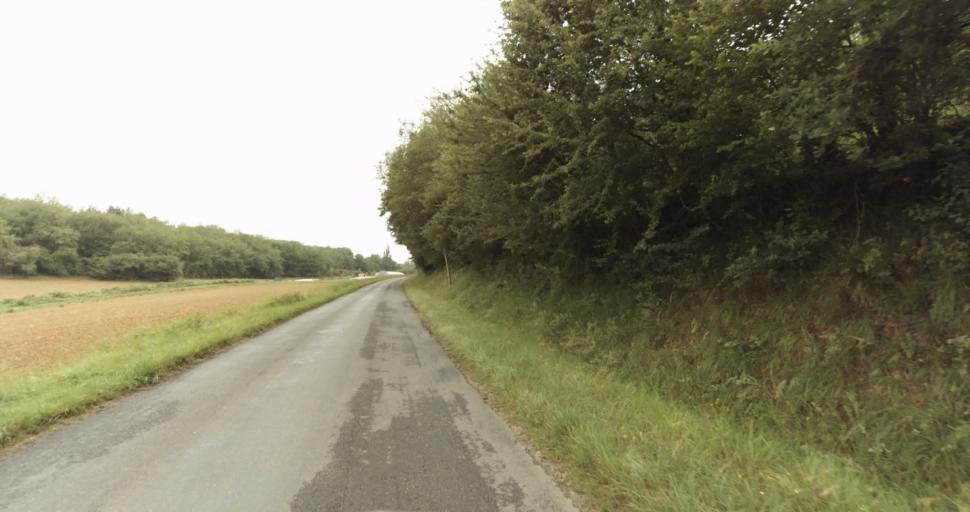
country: FR
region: Aquitaine
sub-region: Departement de la Dordogne
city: Lalinde
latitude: 44.8811
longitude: 0.7770
